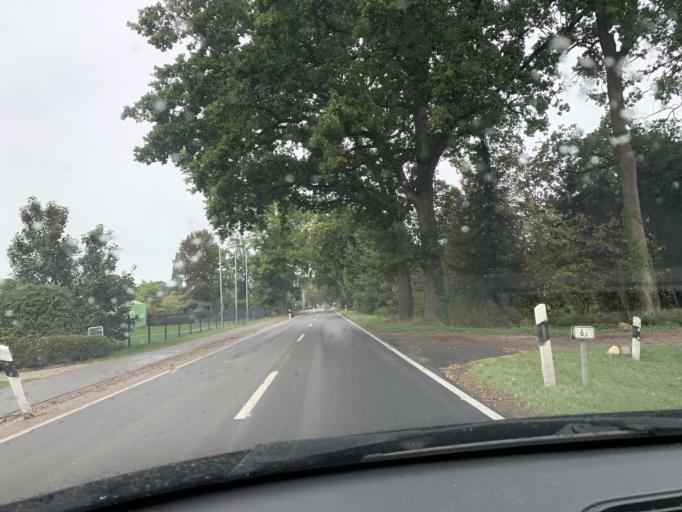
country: DE
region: Lower Saxony
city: Bad Zwischenahn
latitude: 53.1591
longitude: 8.0836
